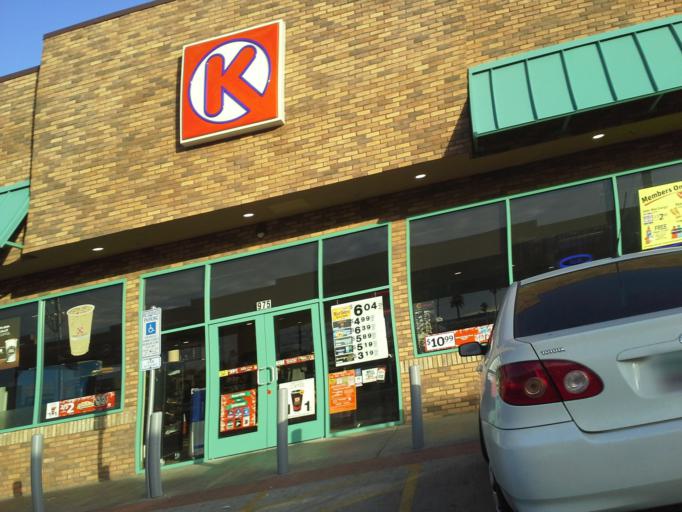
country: US
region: Arizona
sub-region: Maricopa County
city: Phoenix
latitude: 33.4582
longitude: -112.0647
